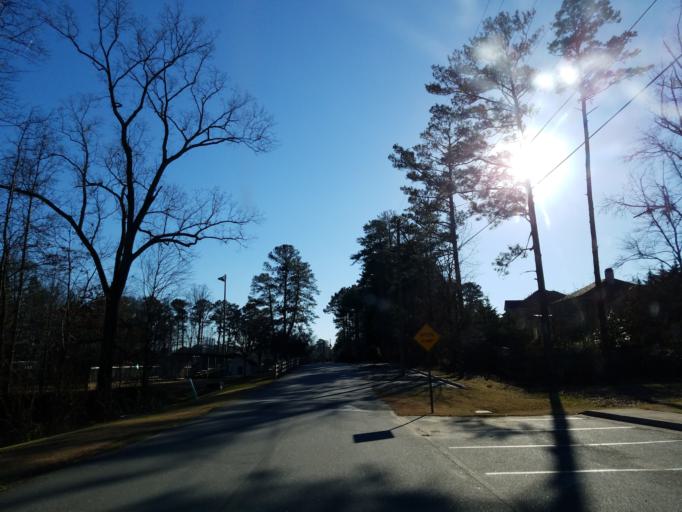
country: US
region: Georgia
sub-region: Cobb County
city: Marietta
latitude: 33.9530
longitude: -84.4911
